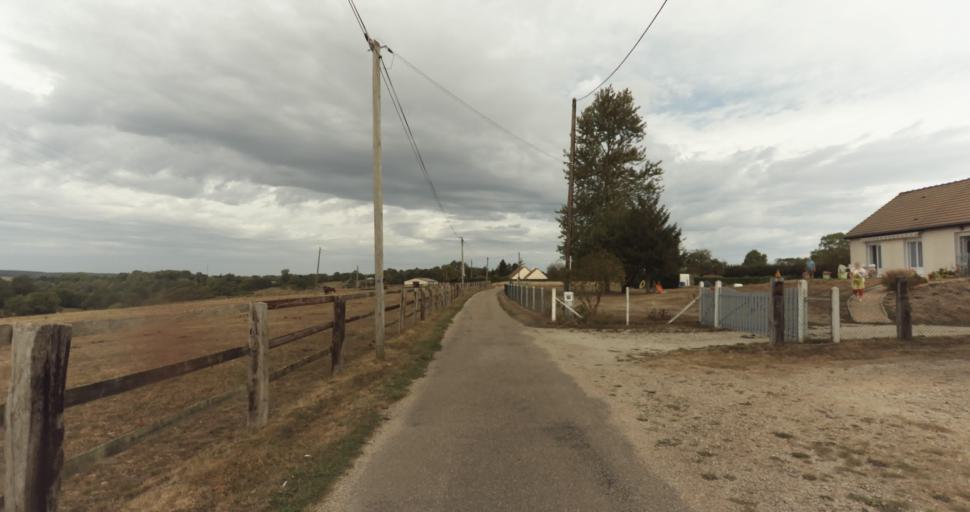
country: FR
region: Lower Normandy
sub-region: Departement de l'Orne
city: Vimoutiers
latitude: 48.9273
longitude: 0.2339
